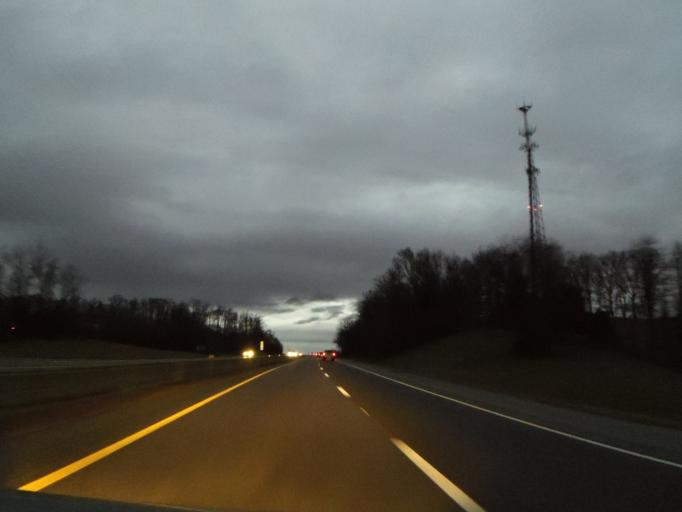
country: US
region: Tennessee
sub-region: Washington County
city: Gray
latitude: 36.4274
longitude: -82.5162
